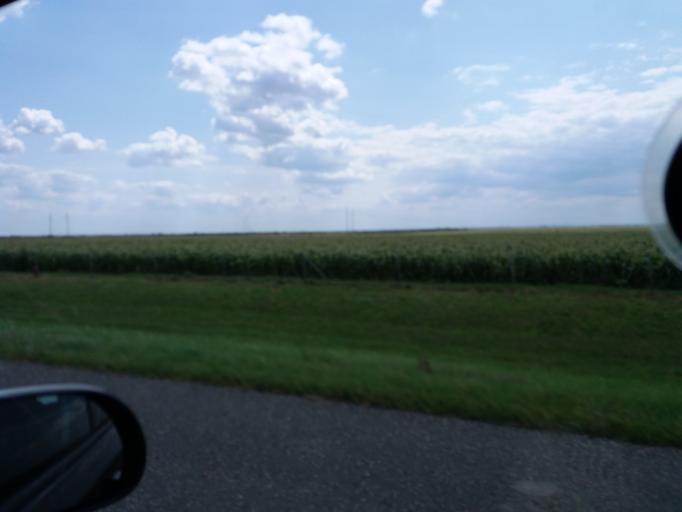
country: RS
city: Budanovci
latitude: 44.9424
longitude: 19.8727
